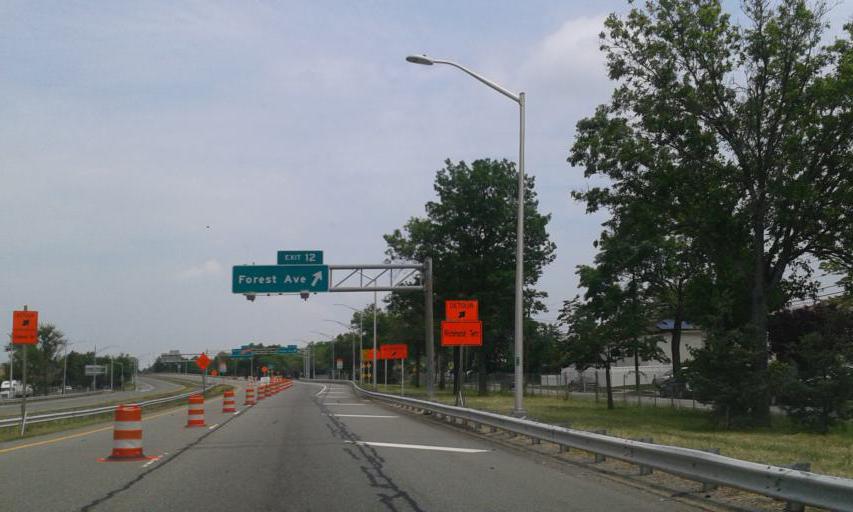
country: US
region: New York
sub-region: Richmond County
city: Bloomfield
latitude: 40.6206
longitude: -74.1490
